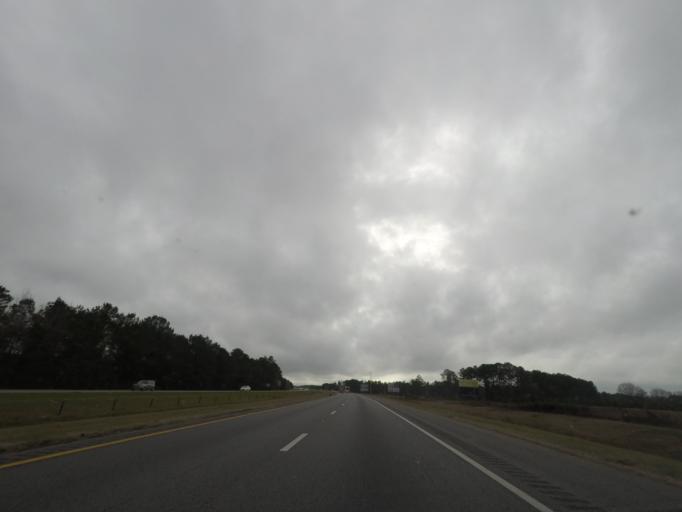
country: US
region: South Carolina
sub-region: Orangeburg County
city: Holly Hill
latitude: 33.3993
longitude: -80.5119
